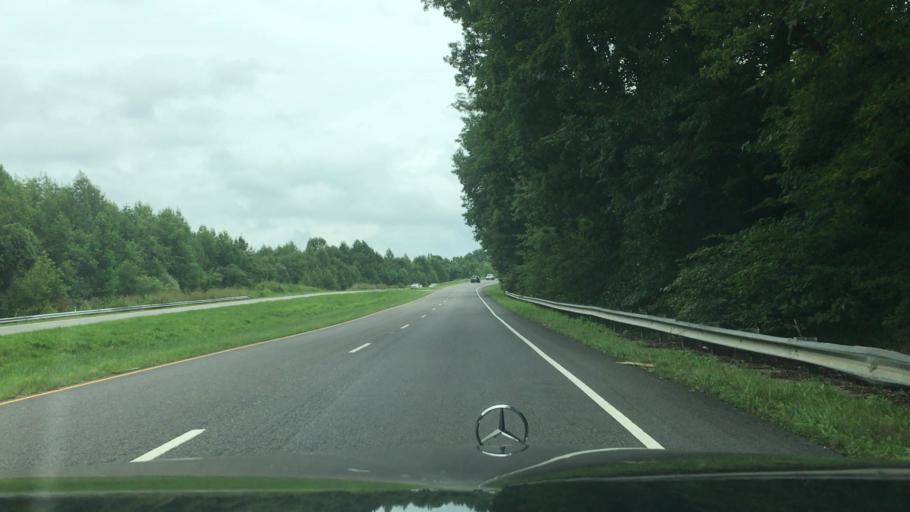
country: US
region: Virginia
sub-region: Amelia County
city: Amelia Court House
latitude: 37.3362
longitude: -78.0070
